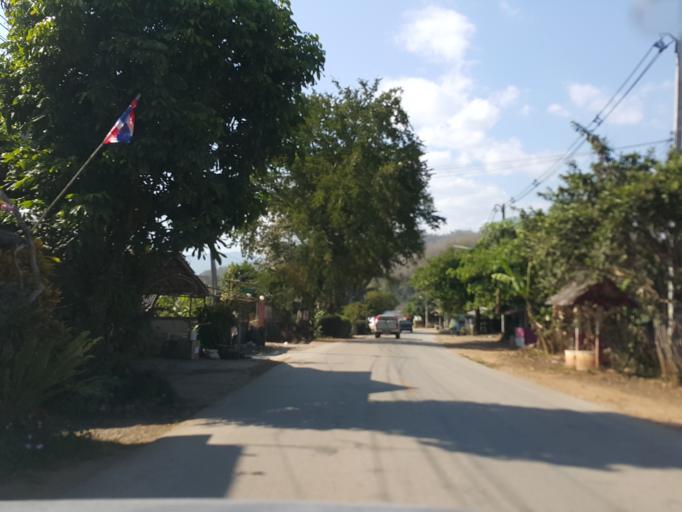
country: TH
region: Chiang Mai
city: Mae Wang
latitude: 18.6536
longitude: 98.6897
